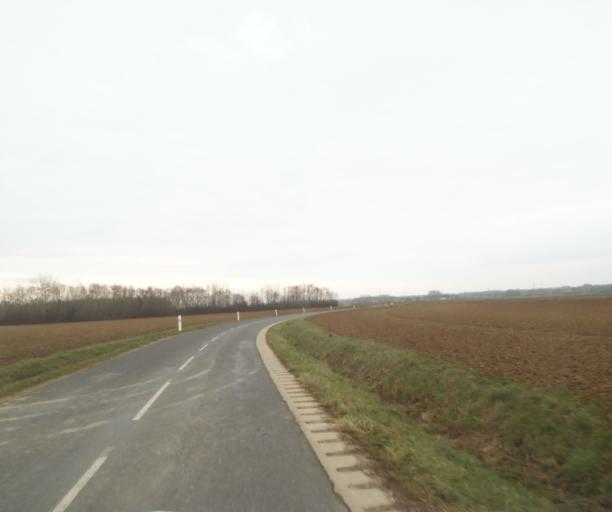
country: FR
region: Champagne-Ardenne
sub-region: Departement de la Haute-Marne
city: Villiers-en-Lieu
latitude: 48.6316
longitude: 4.7723
